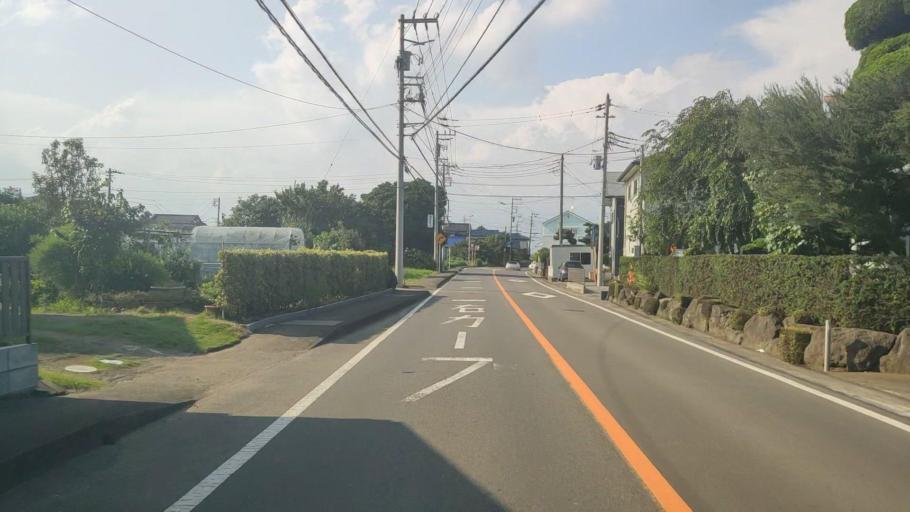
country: JP
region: Kanagawa
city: Isehara
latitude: 35.3703
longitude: 139.3284
